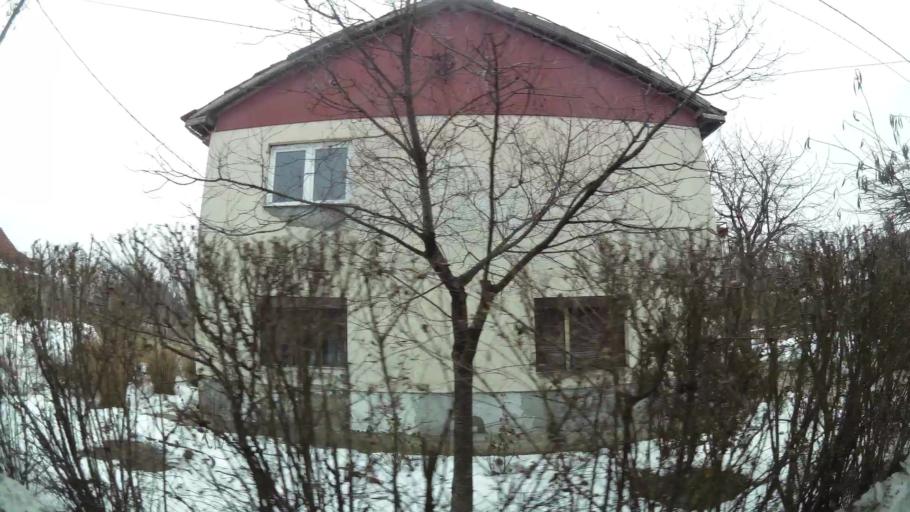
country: MK
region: Saraj
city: Saraj
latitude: 42.0487
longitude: 21.3592
